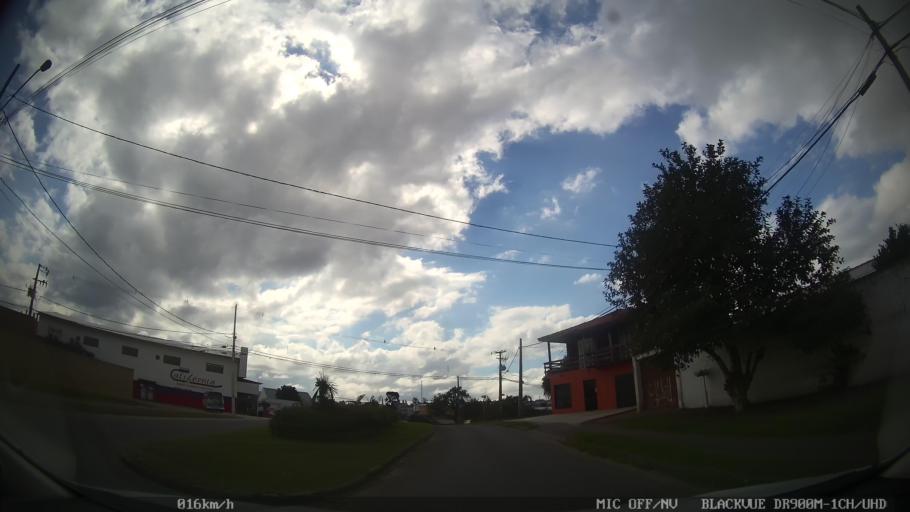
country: BR
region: Parana
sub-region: Colombo
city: Colombo
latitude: -25.3602
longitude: -49.1910
